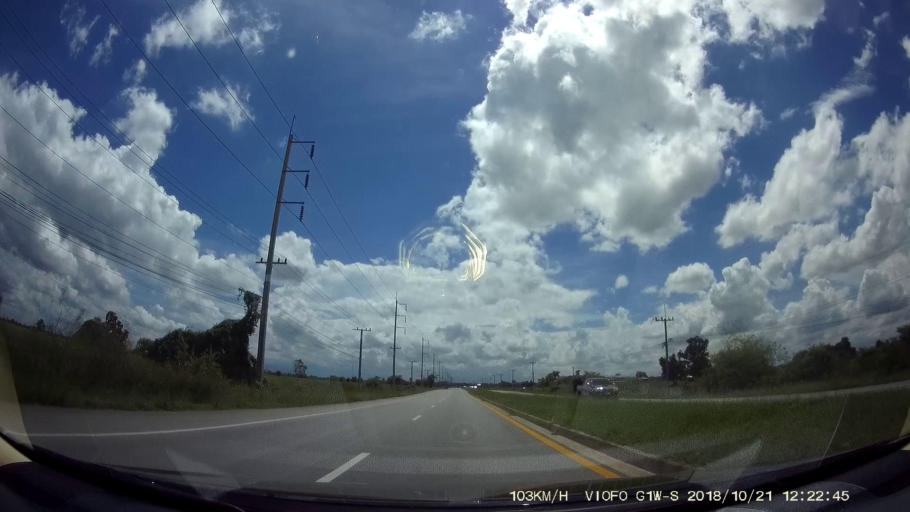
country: TH
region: Nakhon Ratchasima
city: Dan Khun Thot
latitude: 15.2562
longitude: 101.7892
